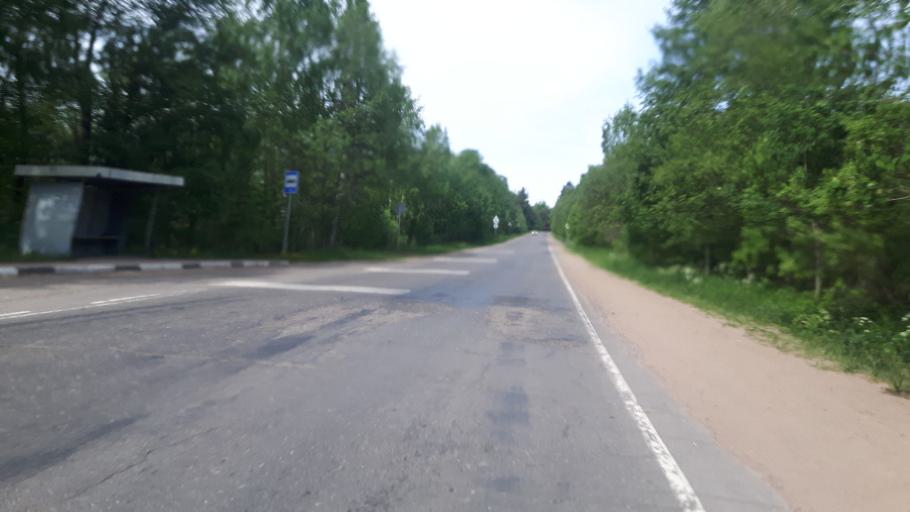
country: RU
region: Leningrad
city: Ust'-Luga
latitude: 59.6459
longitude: 28.2678
